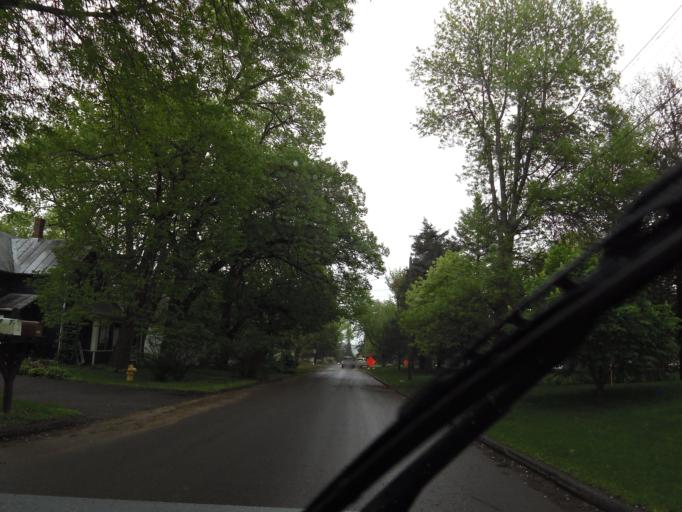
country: US
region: Minnesota
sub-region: Washington County
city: Oak Park Heights
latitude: 45.0392
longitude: -92.8010
